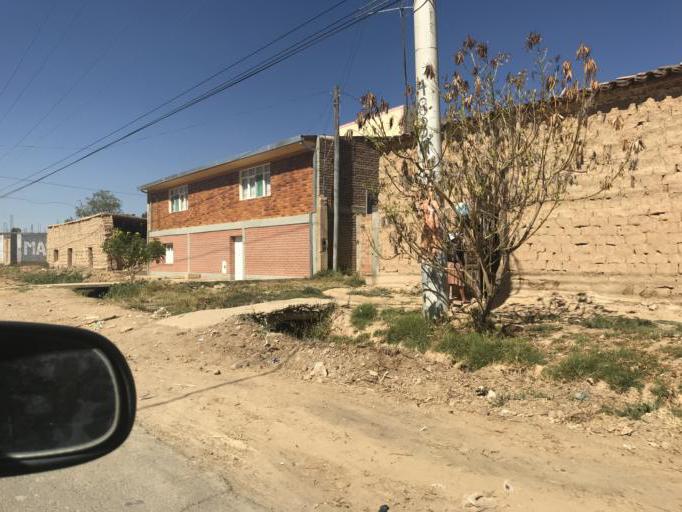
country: BO
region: Cochabamba
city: Cliza
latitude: -17.5961
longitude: -65.9509
